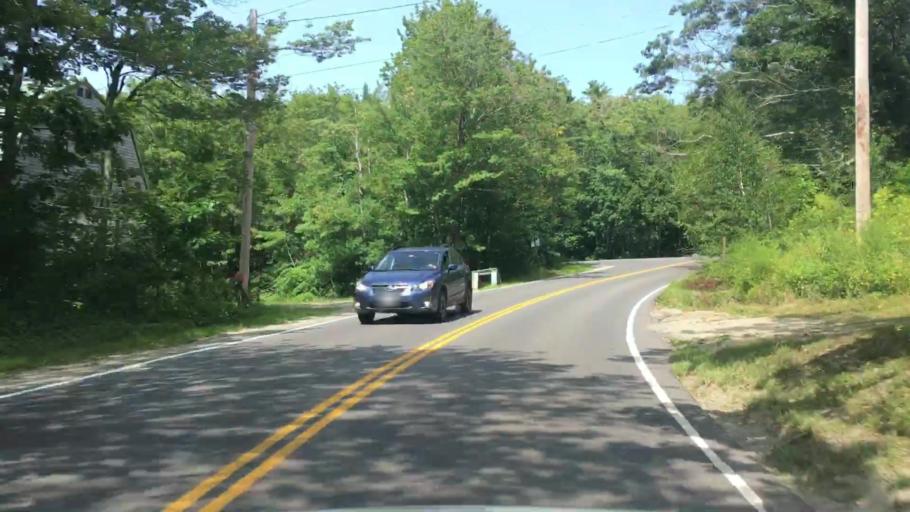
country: US
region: Maine
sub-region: Lincoln County
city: Boothbay
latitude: 43.8735
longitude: -69.6395
